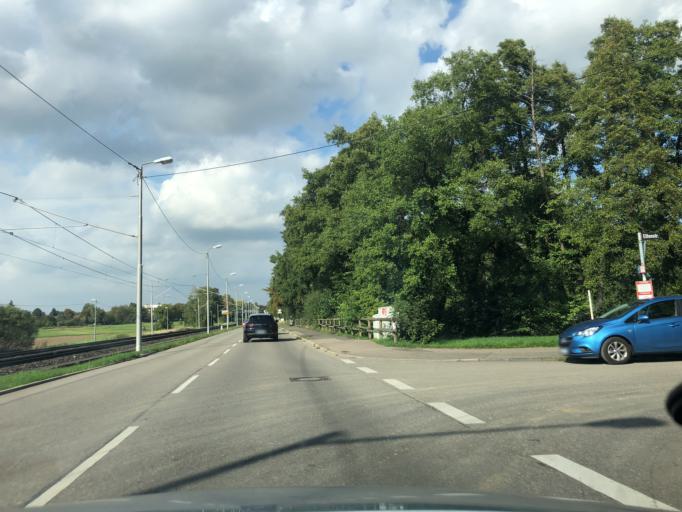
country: DE
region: Baden-Wuerttemberg
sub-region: Regierungsbezirk Stuttgart
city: Leinfelden-Echterdingen
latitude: 48.7341
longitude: 9.1511
